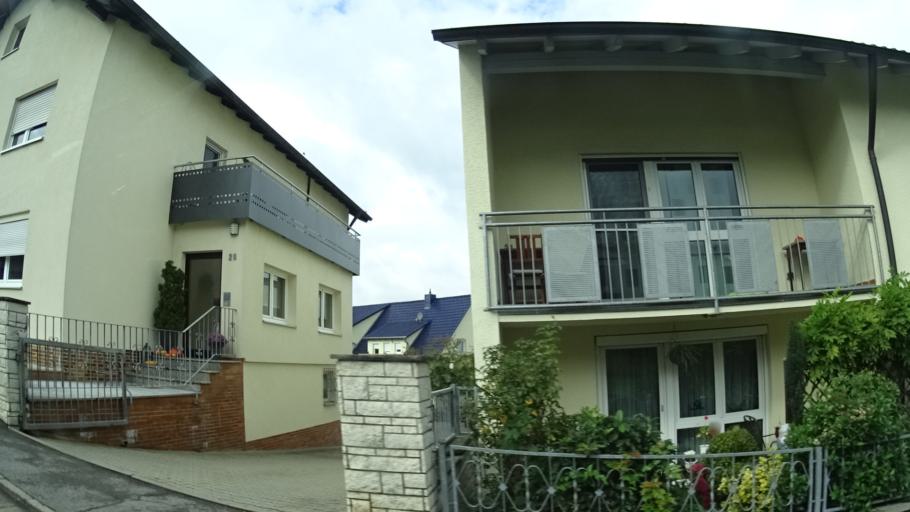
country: DE
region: Bavaria
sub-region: Upper Franconia
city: Viereth-Trunstadt
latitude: 49.9256
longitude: 10.7455
